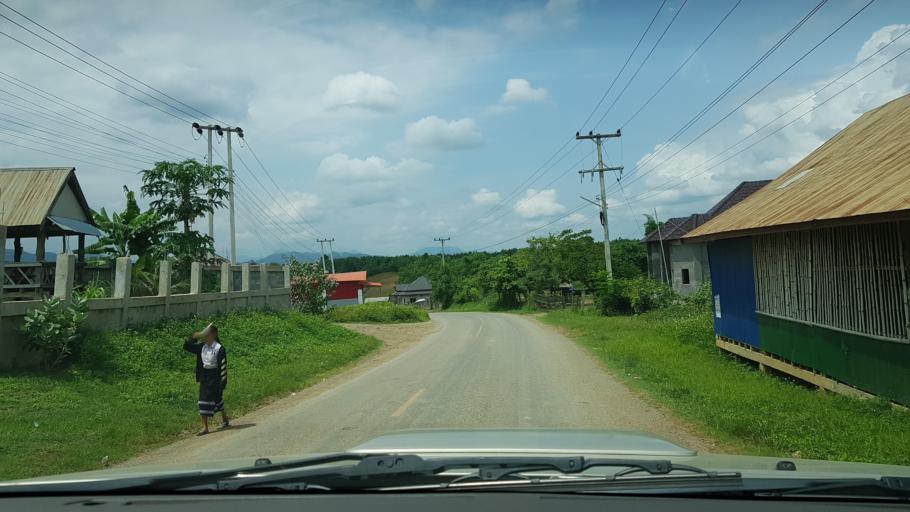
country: LA
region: Loungnamtha
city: Muang Nale
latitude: 20.0335
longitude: 101.3466
